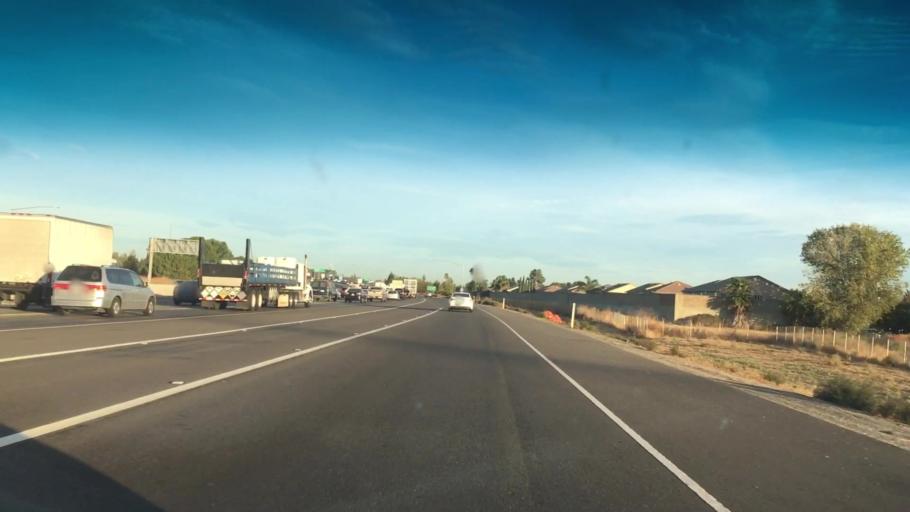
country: US
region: California
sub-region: Sacramento County
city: Parkway
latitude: 38.4694
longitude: -121.4980
